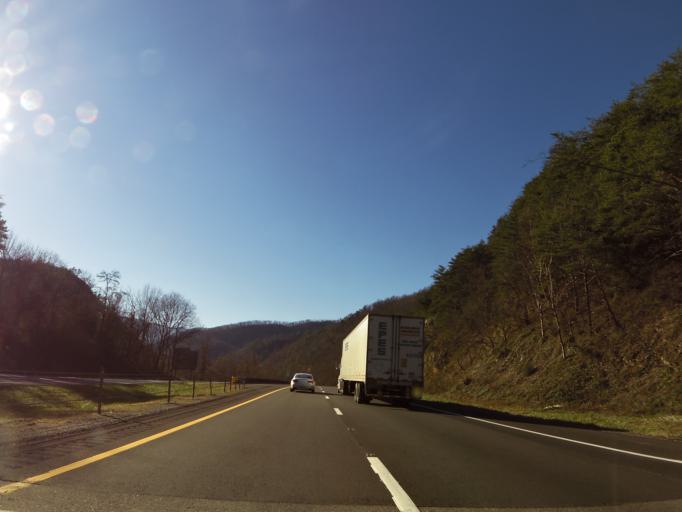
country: US
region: Tennessee
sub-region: Cocke County
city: Newport
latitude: 35.8344
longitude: -83.1818
